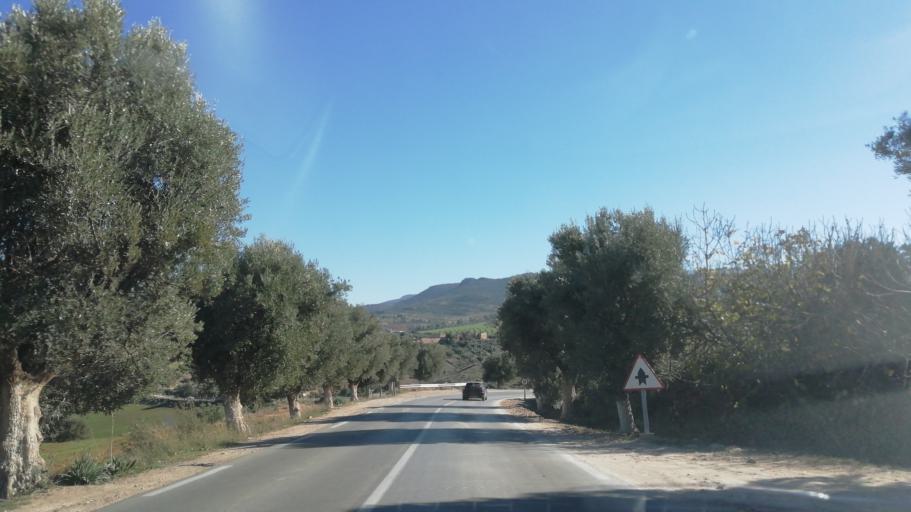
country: DZ
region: Tlemcen
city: Beni Mester
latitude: 34.8305
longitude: -1.5108
